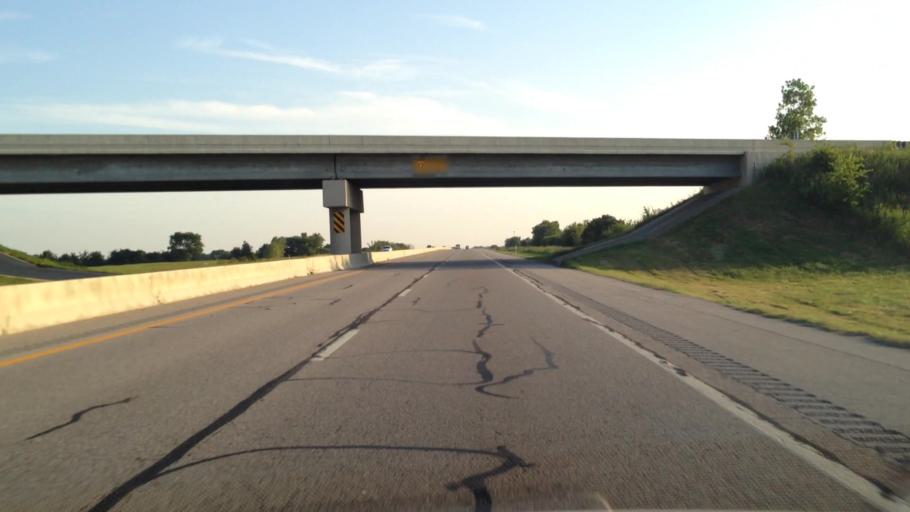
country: US
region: Oklahoma
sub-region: Ottawa County
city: Fairland
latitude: 36.8015
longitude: -94.8802
